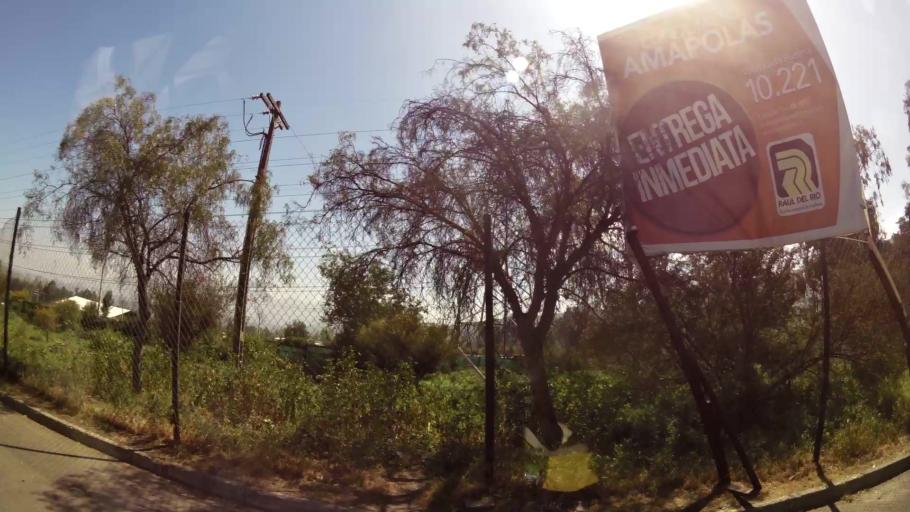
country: CL
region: Santiago Metropolitan
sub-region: Provincia de Santiago
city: Villa Presidente Frei, Nunoa, Santiago, Chile
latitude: -33.4317
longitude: -70.5243
